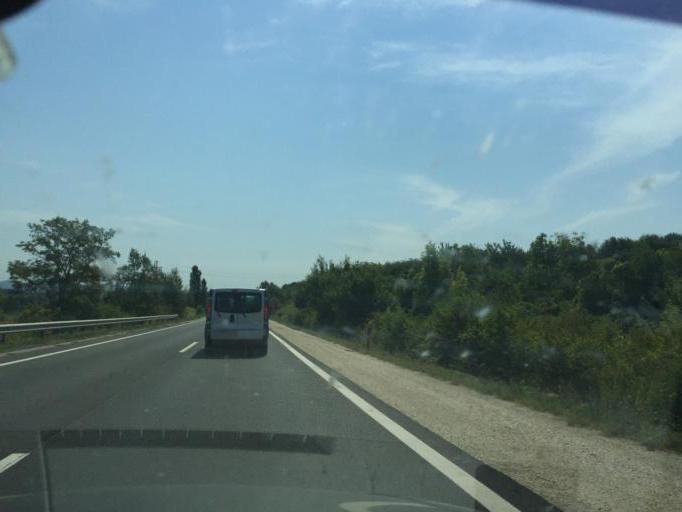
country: HU
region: Pest
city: Kosd
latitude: 47.7896
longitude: 19.1604
